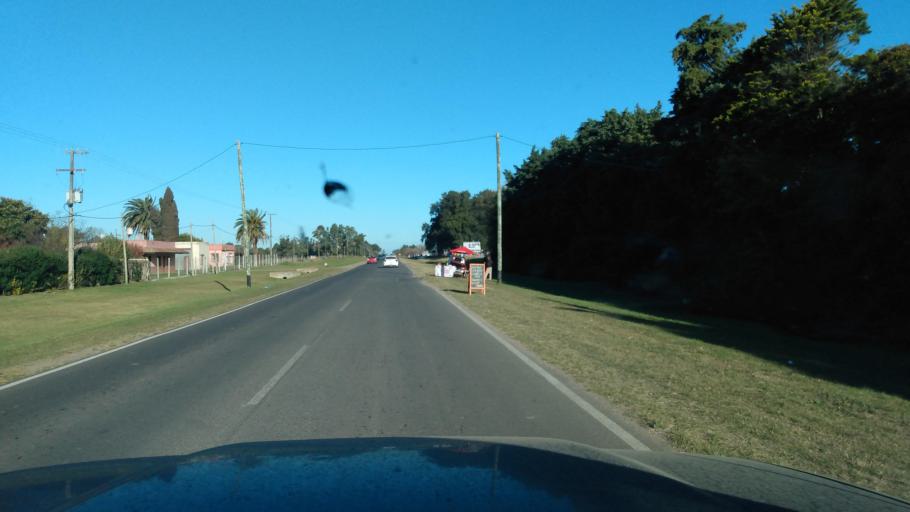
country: AR
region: Buenos Aires
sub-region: Partido de Lujan
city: Lujan
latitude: -34.5088
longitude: -59.1849
